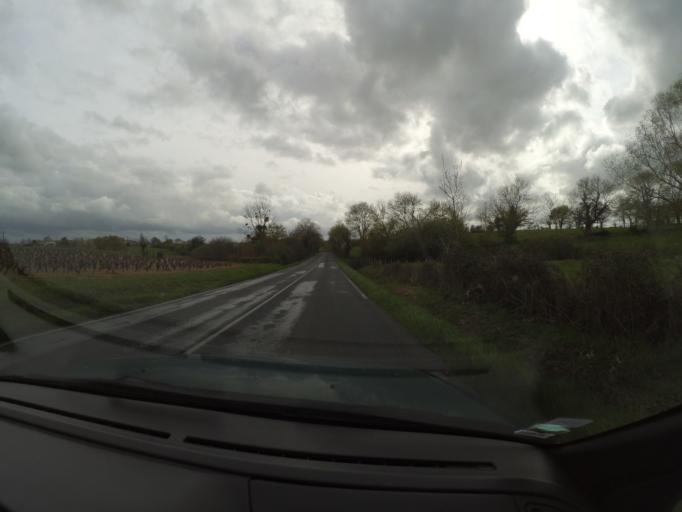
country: FR
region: Pays de la Loire
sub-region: Departement de Maine-et-Loire
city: Saint-Laurent-des-Autels
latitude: 47.3072
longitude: -1.1619
